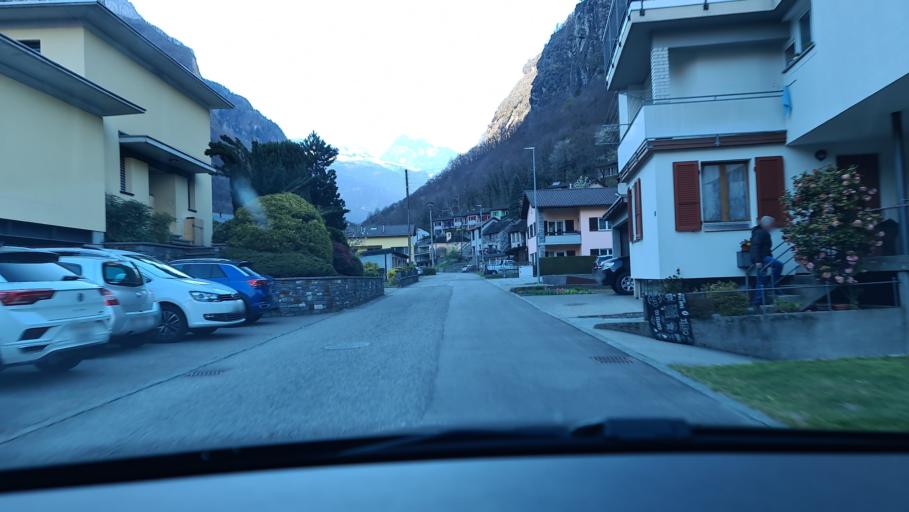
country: CH
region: Ticino
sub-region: Vallemaggia District
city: Cevio
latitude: 46.3456
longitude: 8.6050
